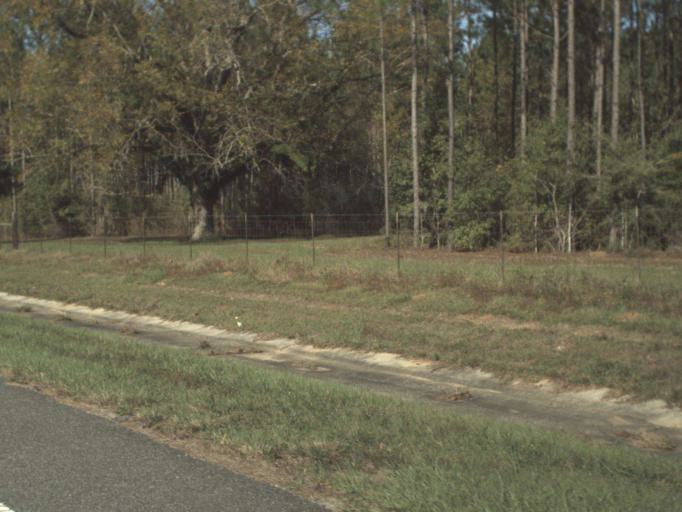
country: US
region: Florida
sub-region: Okaloosa County
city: Crestview
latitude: 30.8134
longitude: -86.7112
